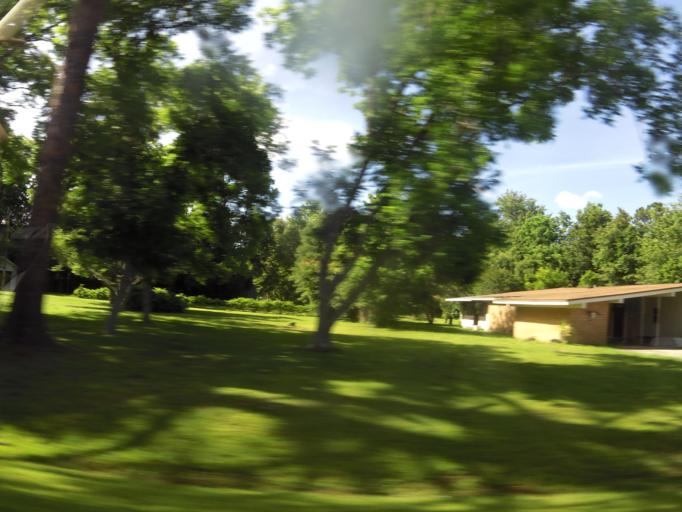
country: US
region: Florida
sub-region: Nassau County
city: Callahan
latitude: 30.5589
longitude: -81.8622
